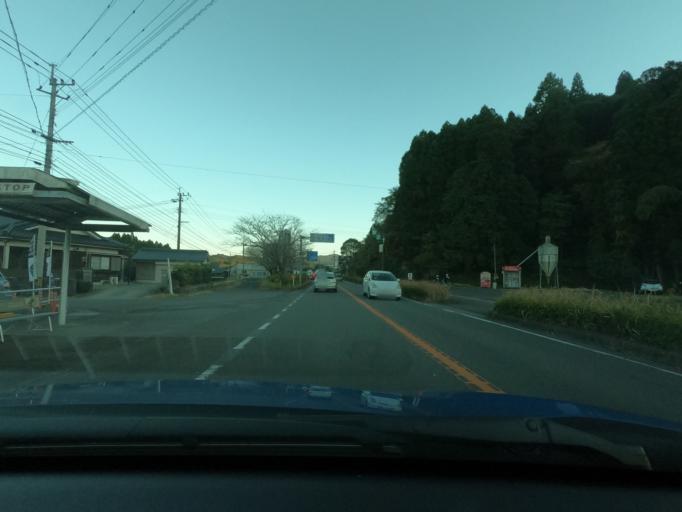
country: JP
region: Kagoshima
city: Satsumasendai
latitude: 31.7972
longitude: 130.4036
